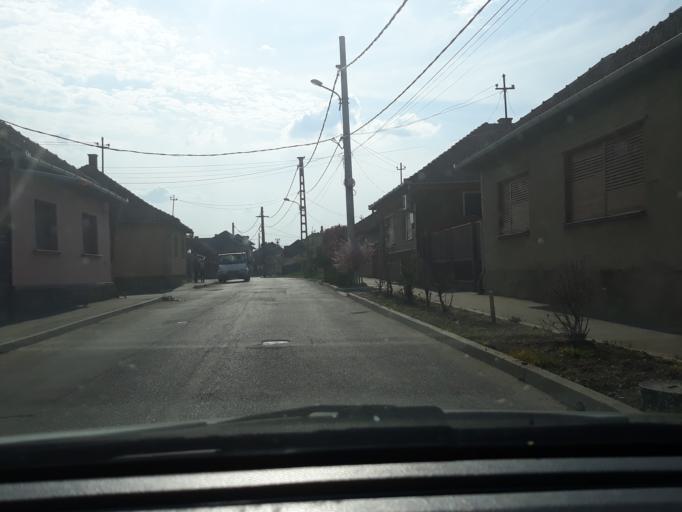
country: RO
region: Bihor
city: Margita
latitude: 47.3508
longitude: 22.3408
